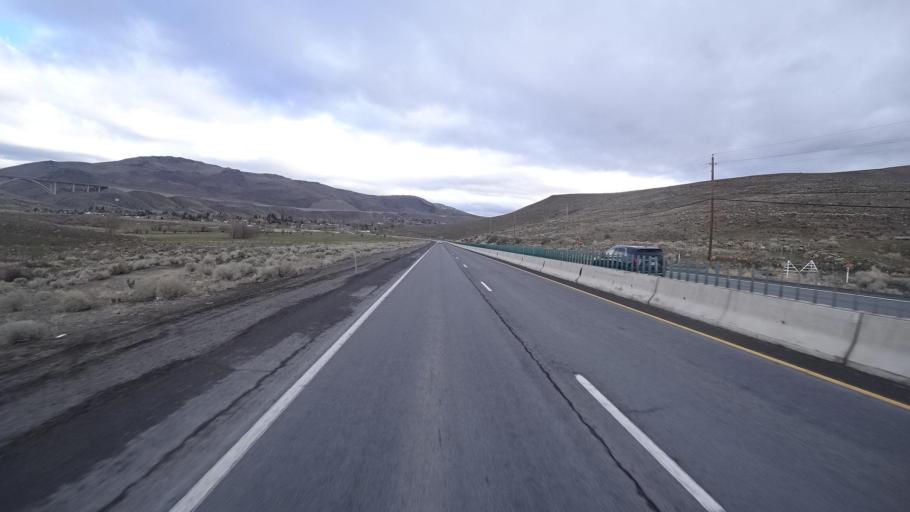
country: US
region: Nevada
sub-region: Storey County
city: Virginia City
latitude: 39.3383
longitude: -119.7790
